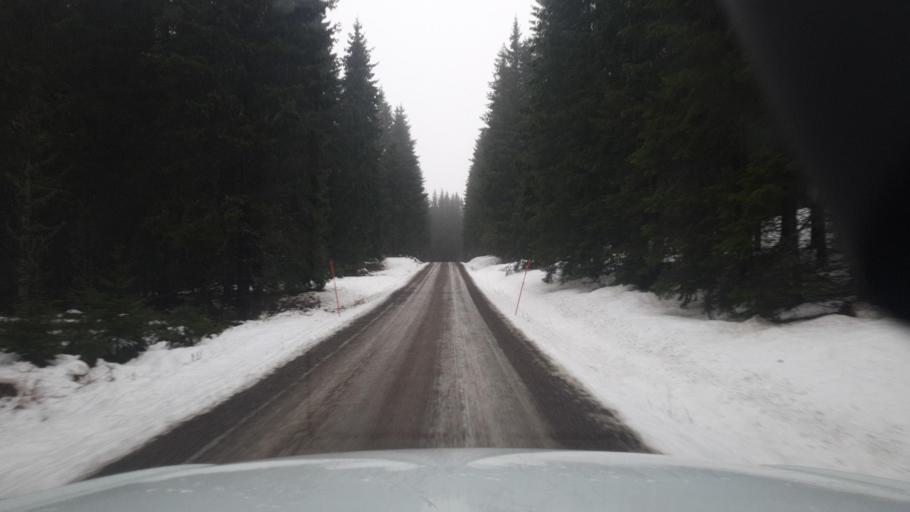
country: SE
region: Vaermland
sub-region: Eda Kommun
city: Charlottenberg
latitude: 60.0370
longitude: 12.6302
